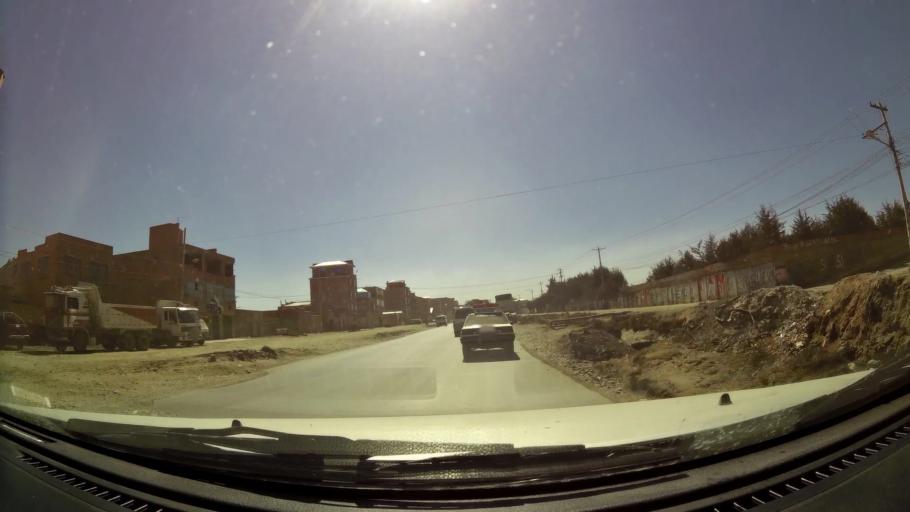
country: BO
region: La Paz
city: La Paz
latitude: -16.5492
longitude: -68.2041
